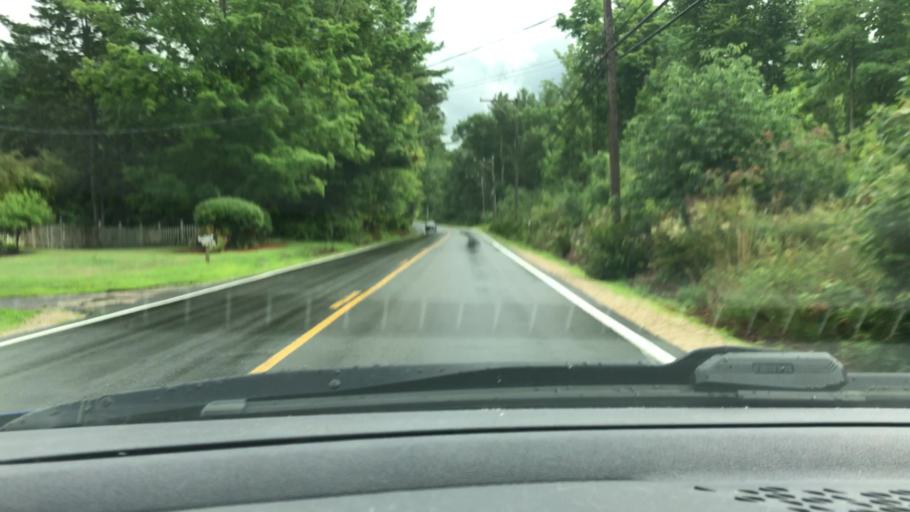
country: US
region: New Hampshire
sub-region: Rockingham County
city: Candia
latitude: 43.1593
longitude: -71.2412
